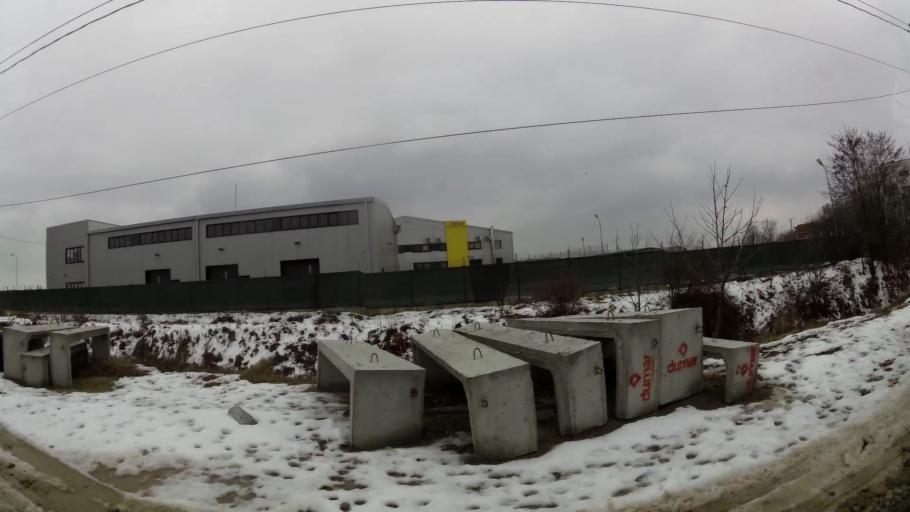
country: RO
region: Ilfov
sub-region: Comuna Otopeni
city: Otopeni
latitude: 44.5483
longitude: 26.0918
